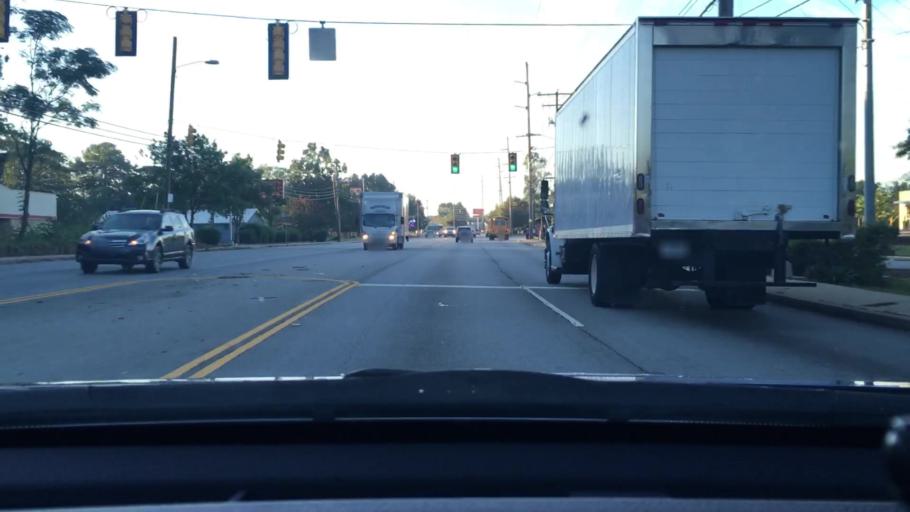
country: US
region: South Carolina
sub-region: Lexington County
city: Saint Andrews
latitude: 34.0571
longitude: -81.1111
